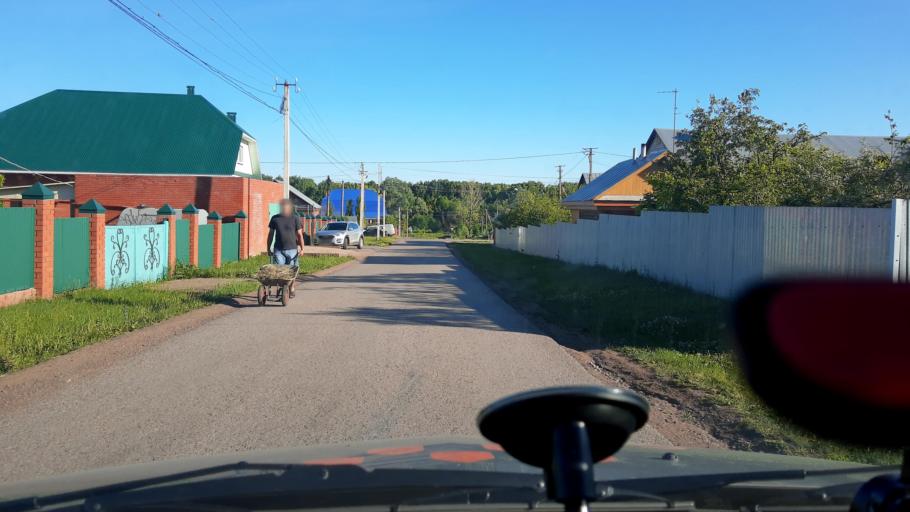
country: RU
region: Bashkortostan
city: Chishmy
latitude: 54.6028
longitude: 55.3776
